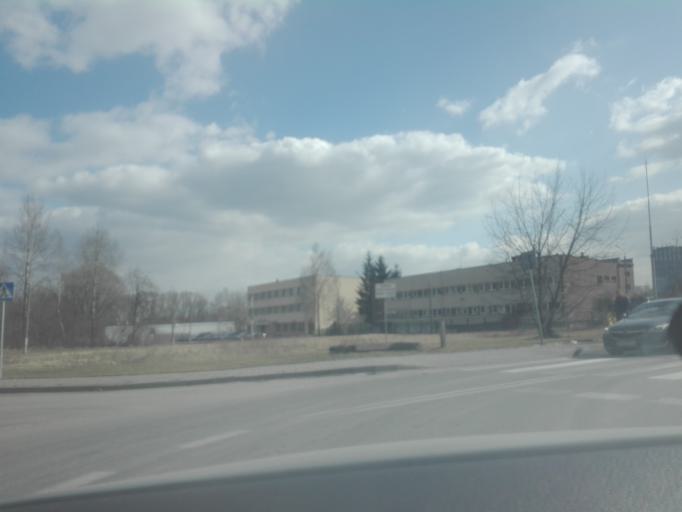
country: PL
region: Silesian Voivodeship
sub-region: Katowice
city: Katowice
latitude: 50.2612
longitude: 18.9969
